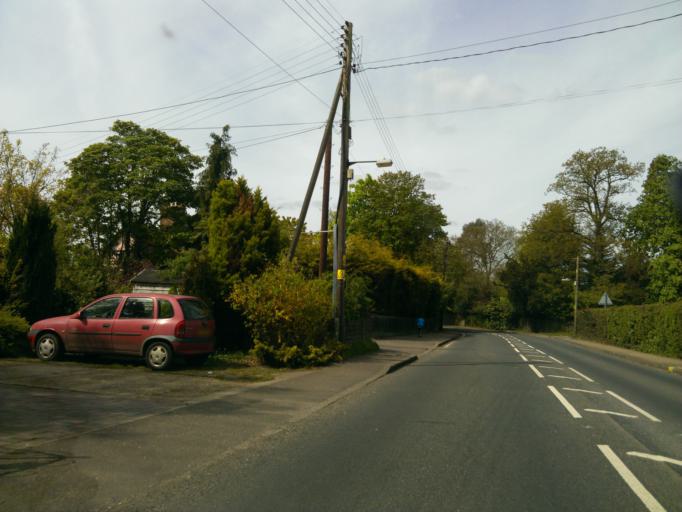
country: GB
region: England
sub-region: Essex
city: Earls Colne
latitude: 51.9286
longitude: 0.6931
